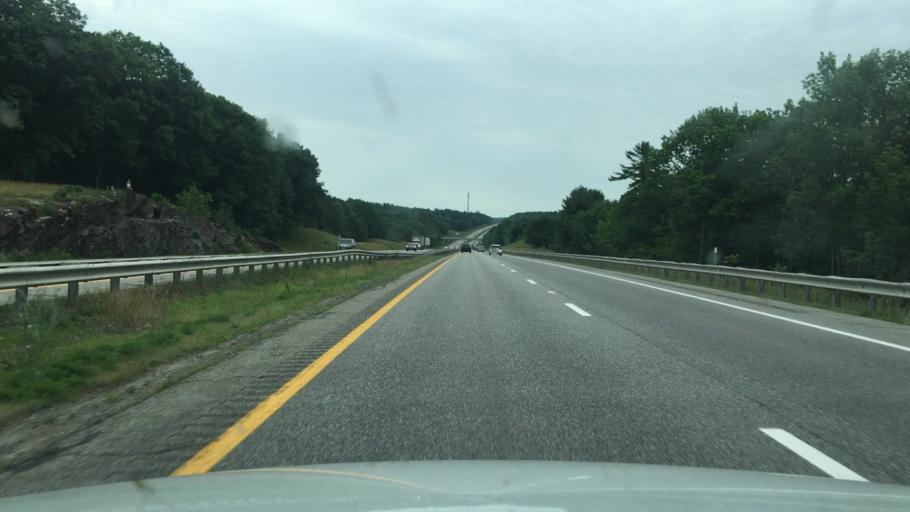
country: US
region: Maine
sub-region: Kennebec County
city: Hallowell
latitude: 44.2854
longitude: -69.8068
